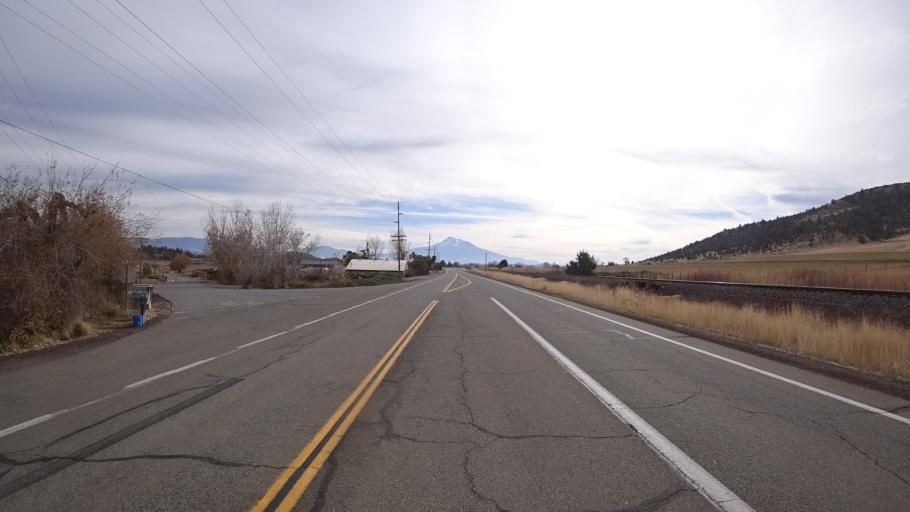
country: US
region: California
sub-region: Siskiyou County
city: Montague
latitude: 41.6835
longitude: -122.5331
